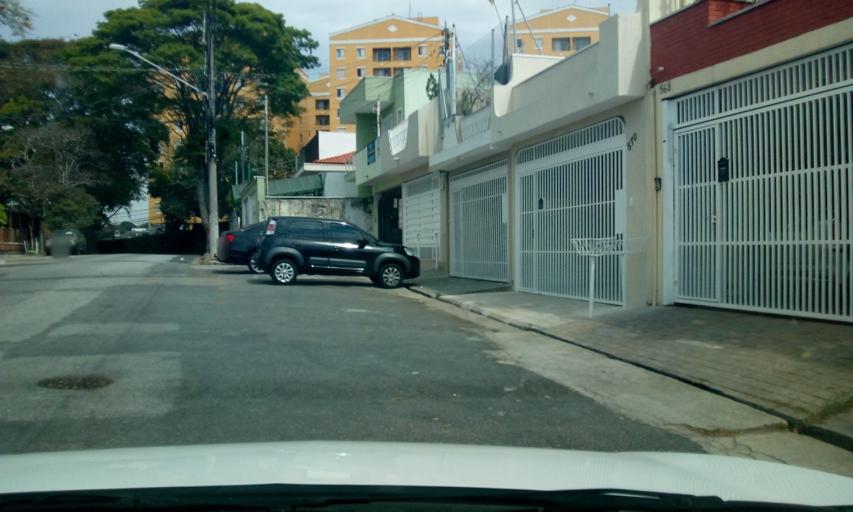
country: BR
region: Sao Paulo
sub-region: Taboao Da Serra
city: Taboao da Serra
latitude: -23.5935
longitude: -46.7270
